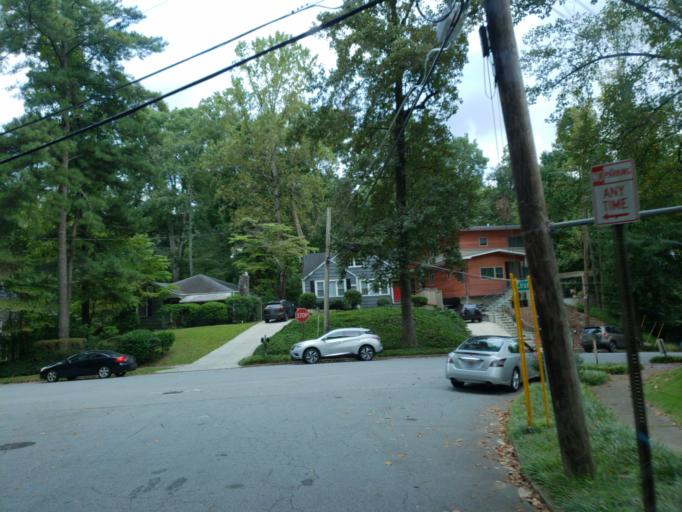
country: US
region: Georgia
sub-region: DeKalb County
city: Druid Hills
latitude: 33.7907
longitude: -84.3612
